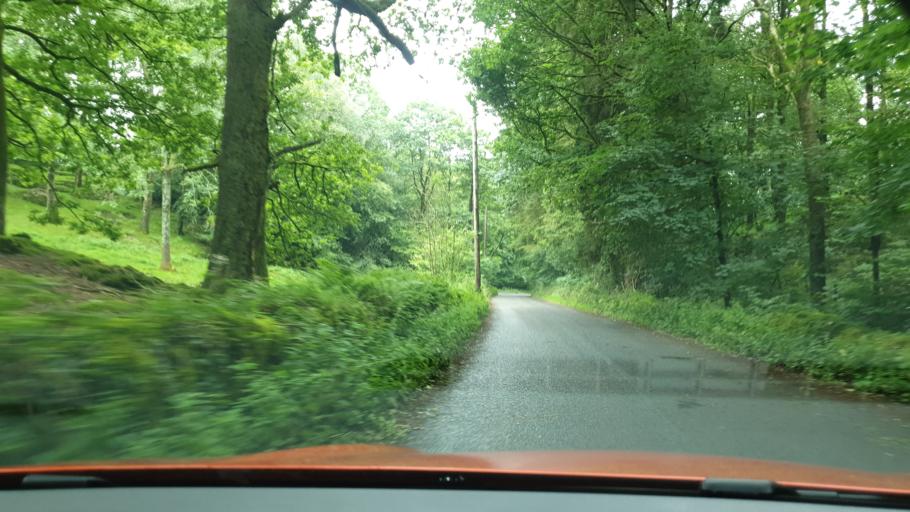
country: GB
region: England
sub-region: Cumbria
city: Grange-over-Sands
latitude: 54.2707
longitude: -2.9867
